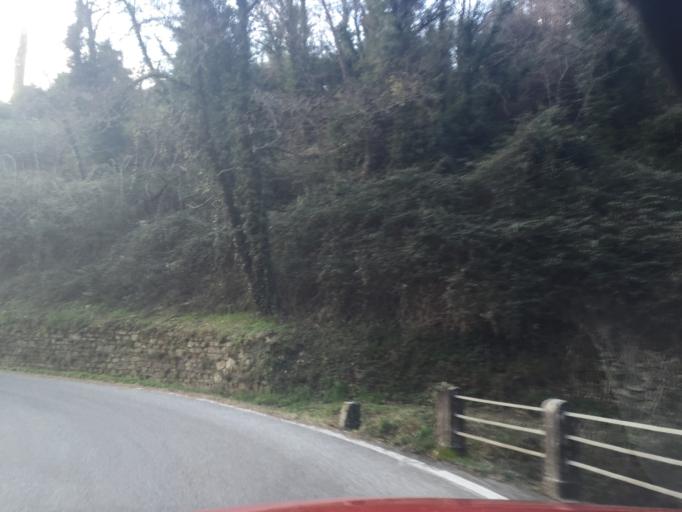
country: IT
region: Tuscany
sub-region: Province of Florence
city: Vinci
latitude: 43.8167
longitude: 10.9302
